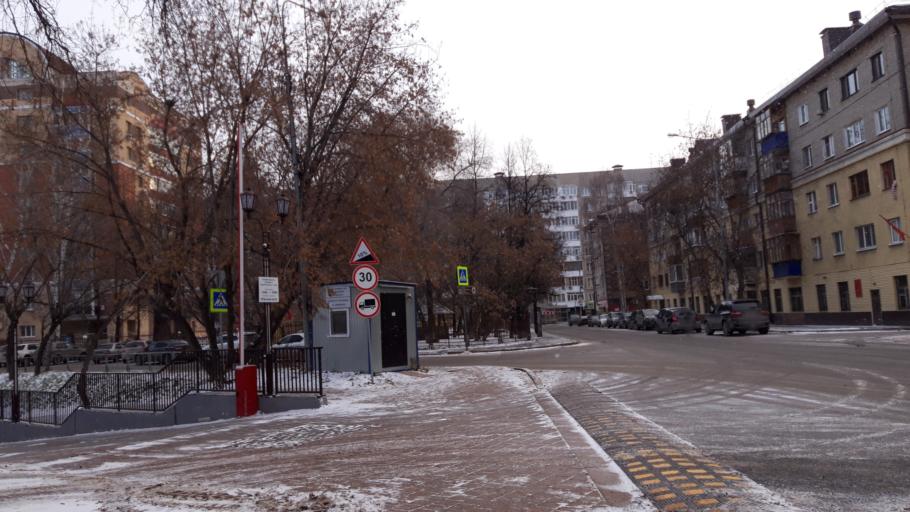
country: RU
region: Tjumen
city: Tyumen
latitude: 57.1602
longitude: 65.5500
